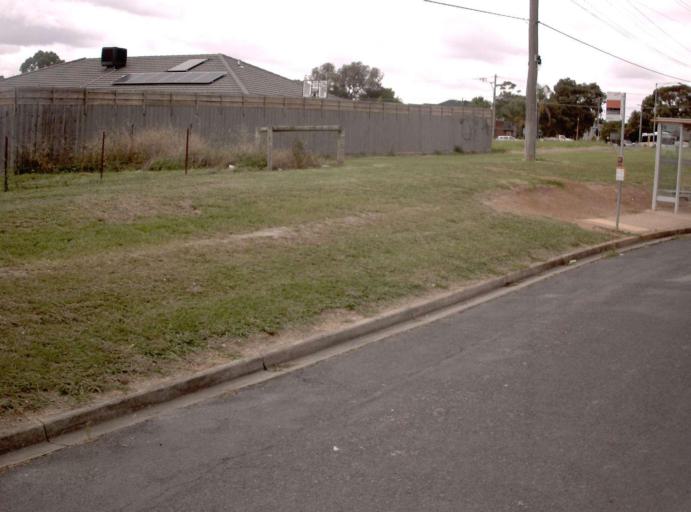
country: AU
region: Victoria
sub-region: Maroondah
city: Croydon North
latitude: -37.7703
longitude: 145.2959
